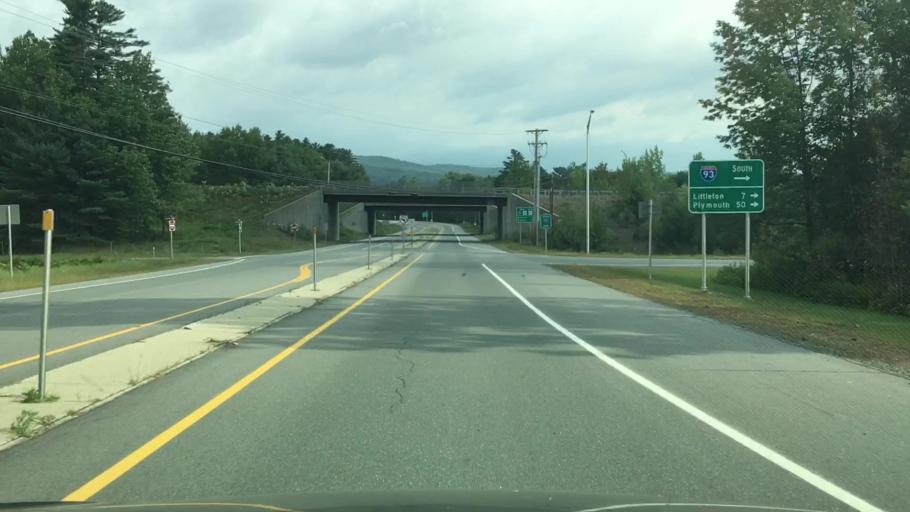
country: US
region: New Hampshire
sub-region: Grafton County
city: Littleton
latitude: 44.3279
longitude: -71.8746
